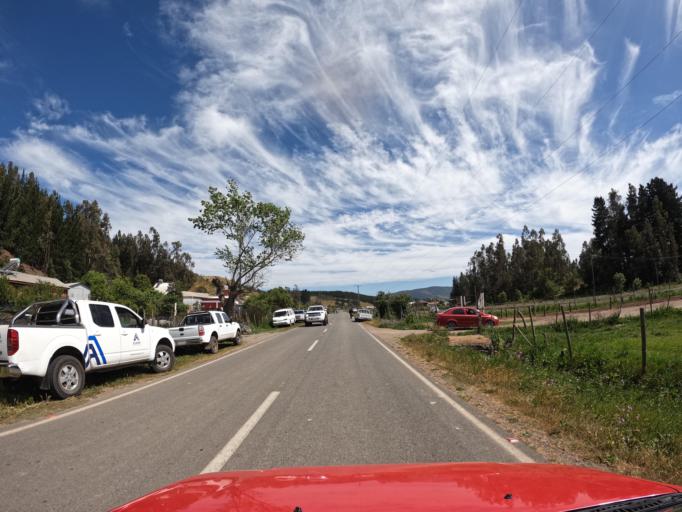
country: CL
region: Maule
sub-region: Provincia de Talca
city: Constitucion
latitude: -35.0161
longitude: -72.0382
